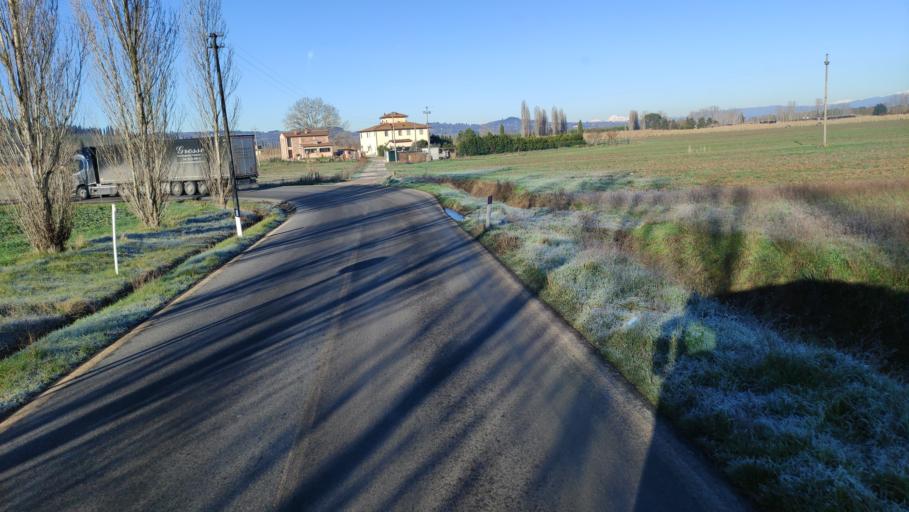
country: IT
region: Tuscany
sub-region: Province of Florence
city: Castelfiorentino
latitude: 43.6475
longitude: 10.9437
